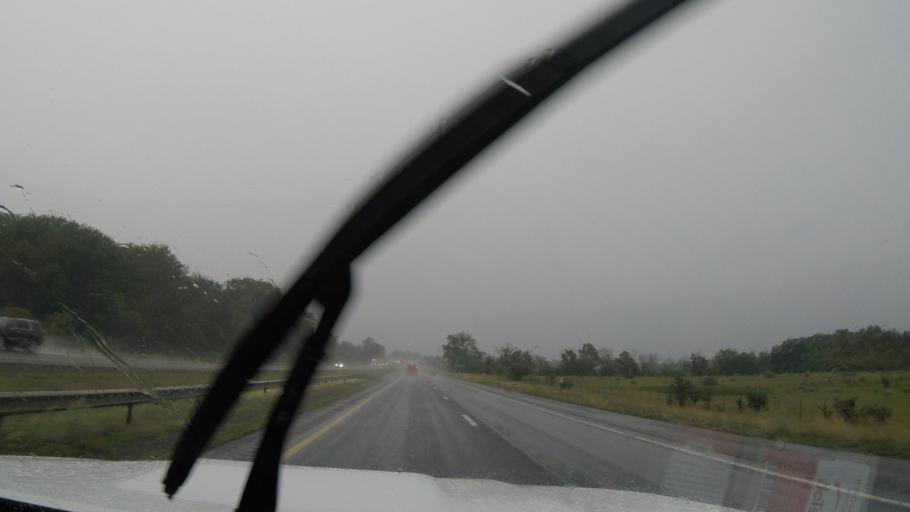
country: US
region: New York
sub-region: Seneca County
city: Seneca Falls
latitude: 42.9834
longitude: -76.7848
